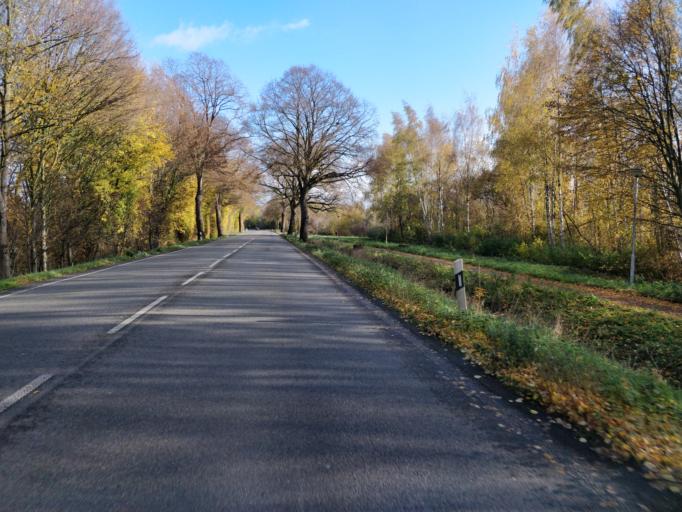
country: DE
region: North Rhine-Westphalia
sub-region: Regierungsbezirk Dusseldorf
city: Emmerich
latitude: 51.8299
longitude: 6.2798
